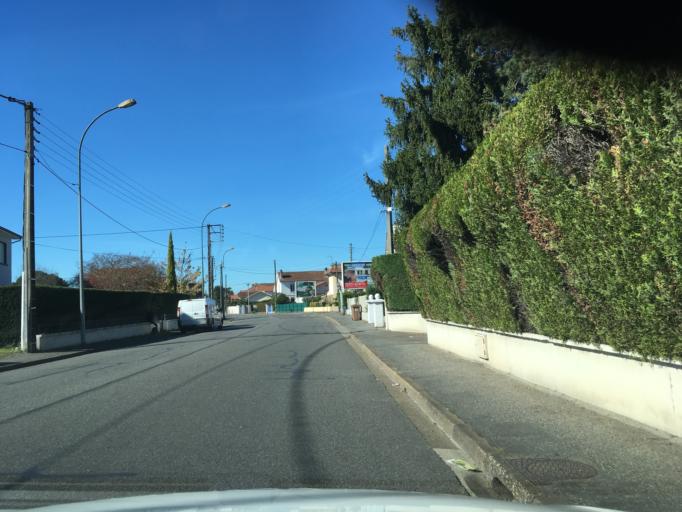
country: FR
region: Aquitaine
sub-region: Departement des Pyrenees-Atlantiques
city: Lons
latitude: 43.3242
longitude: -0.3759
